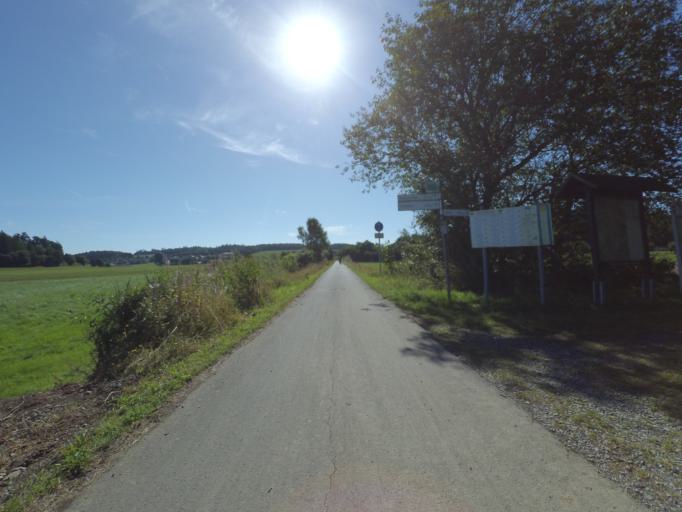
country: DE
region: Rheinland-Pfalz
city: Udler
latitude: 50.1401
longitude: 6.8829
